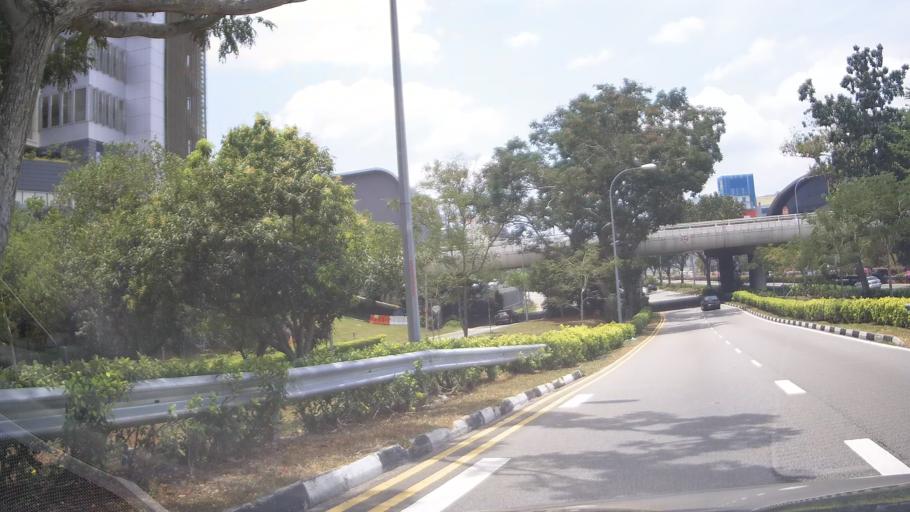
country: SG
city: Singapore
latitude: 1.3419
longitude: 103.9479
